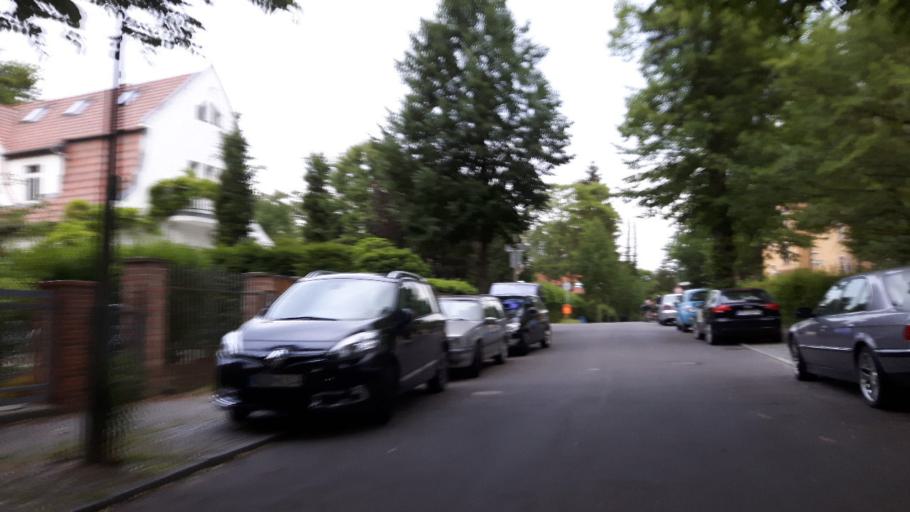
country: DE
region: Berlin
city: Wannsee
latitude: 52.3971
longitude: 13.1441
